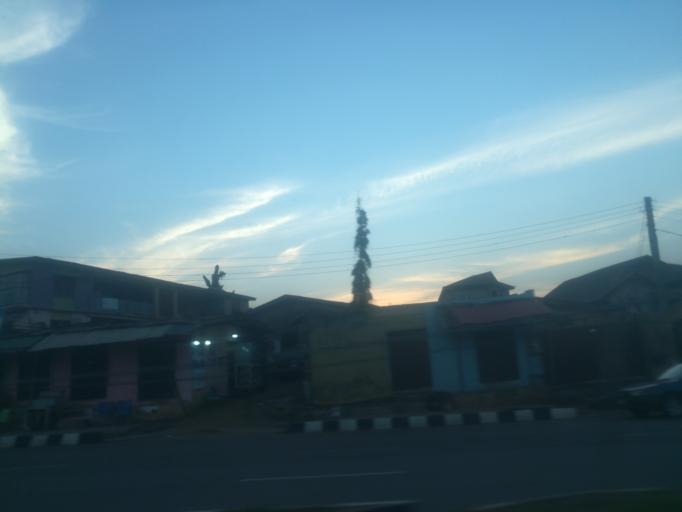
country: NG
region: Ogun
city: Abeokuta
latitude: 7.1380
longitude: 3.3659
